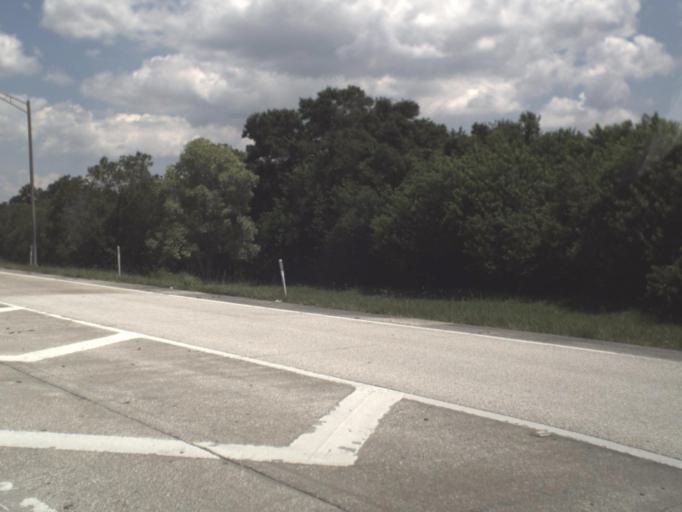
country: US
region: Florida
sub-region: Pinellas County
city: Gulfport
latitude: 27.7421
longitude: -82.6764
